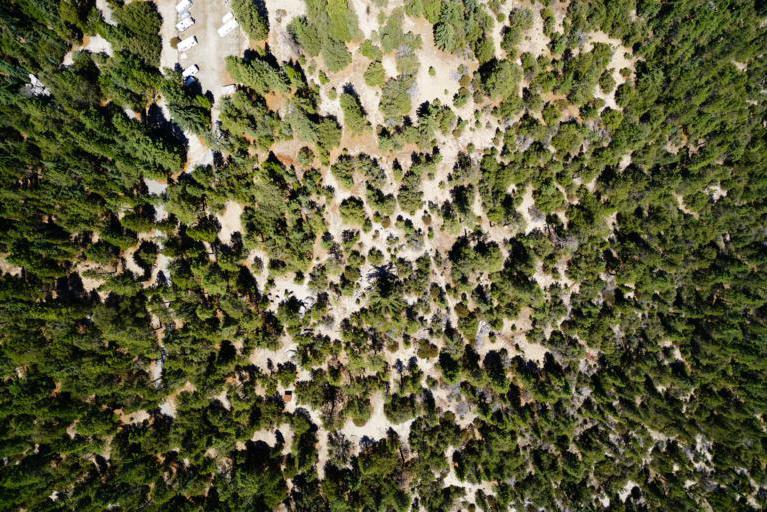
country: US
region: California
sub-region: Riverside County
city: Idyllwild-Pine Cove
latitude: 33.7684
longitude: -116.7260
